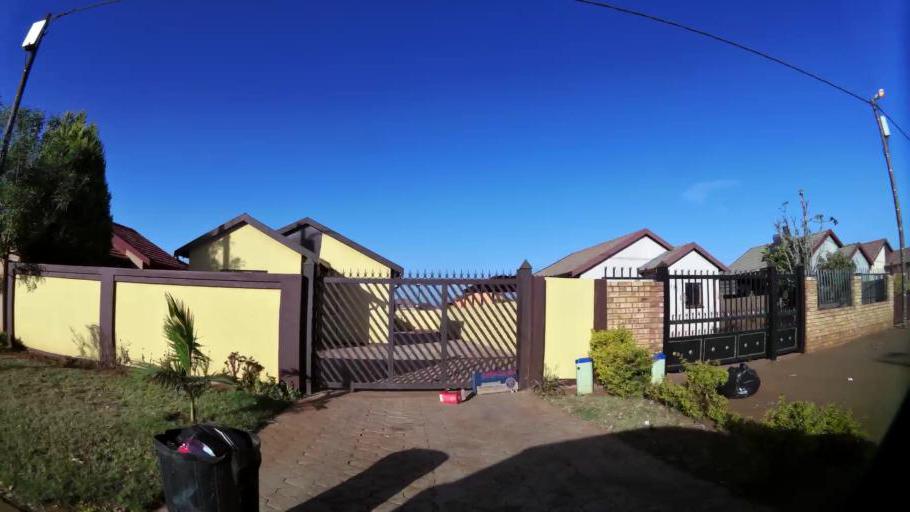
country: ZA
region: Gauteng
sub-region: City of Tshwane Metropolitan Municipality
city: Mabopane
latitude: -25.5971
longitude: 28.1113
